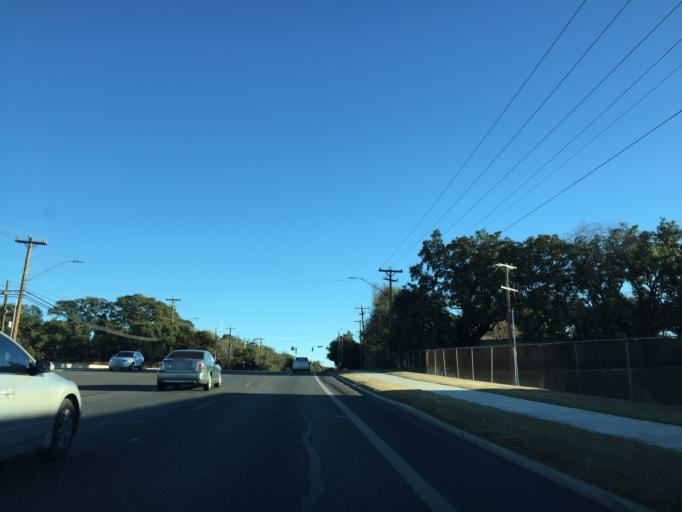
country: US
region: Texas
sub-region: Bexar County
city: Castle Hills
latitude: 29.5450
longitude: -98.5079
